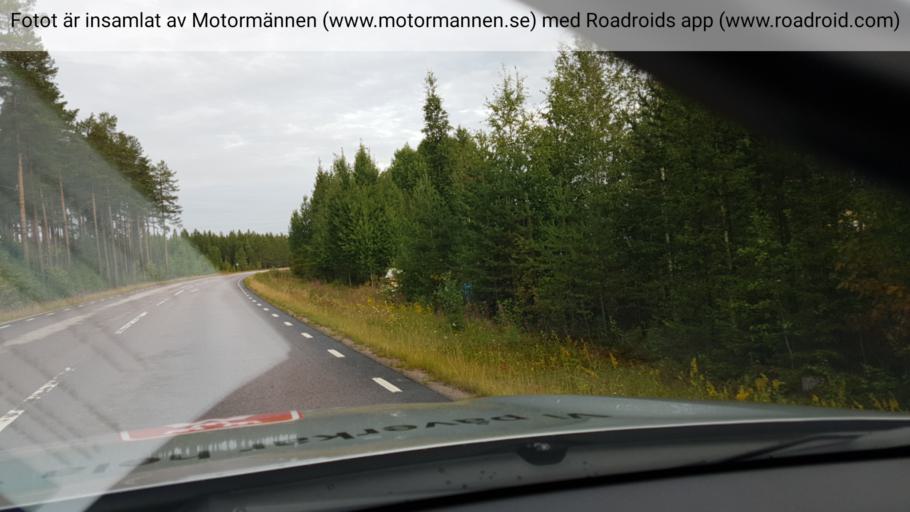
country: SE
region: Norrbotten
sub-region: Lulea Kommun
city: Sodra Sunderbyn
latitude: 65.6271
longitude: 21.9298
